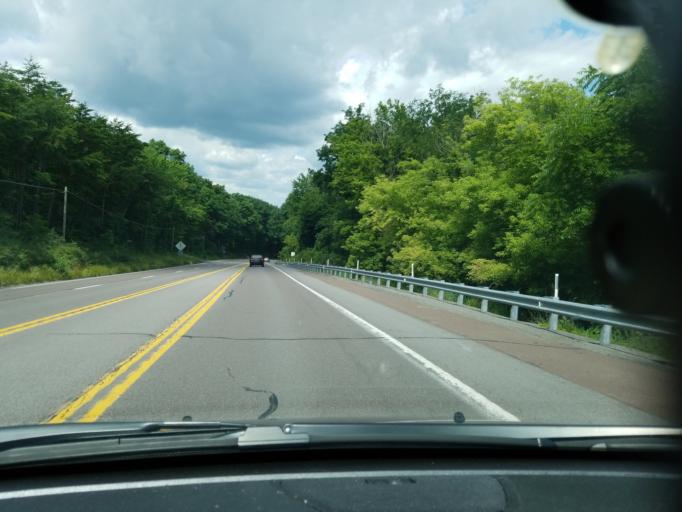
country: US
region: Pennsylvania
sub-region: Northumberland County
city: Elysburg
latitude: 40.8488
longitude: -76.5272
